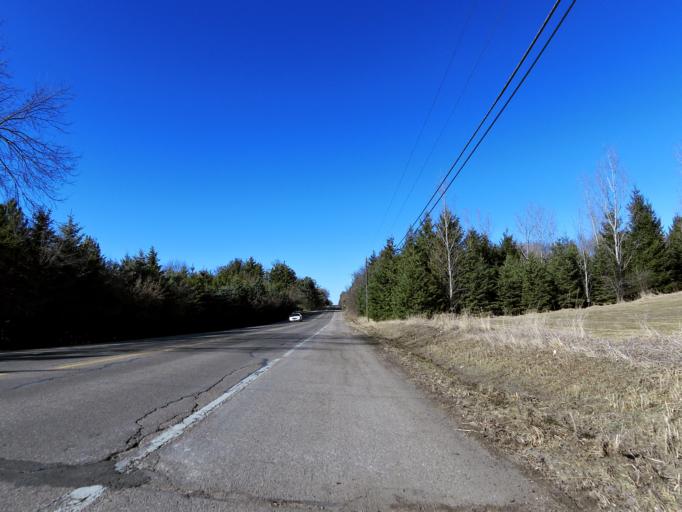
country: US
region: Minnesota
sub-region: Washington County
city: Lakeland
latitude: 44.9766
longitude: -92.8223
